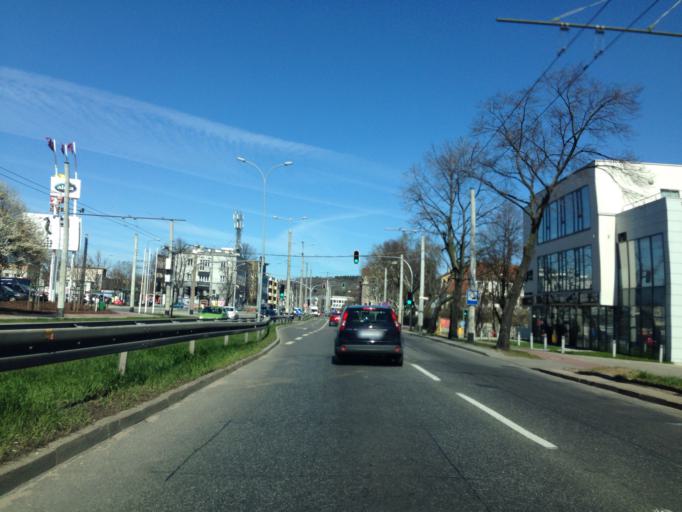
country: PL
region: Pomeranian Voivodeship
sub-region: Sopot
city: Sopot
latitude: 54.4750
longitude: 18.5535
